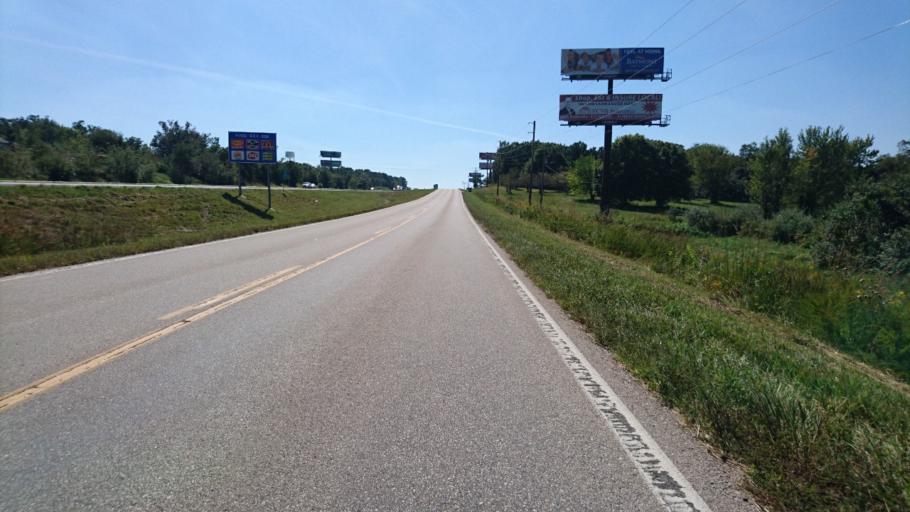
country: US
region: Missouri
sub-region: Franklin County
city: Sullivan
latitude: 38.2328
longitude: -91.1488
